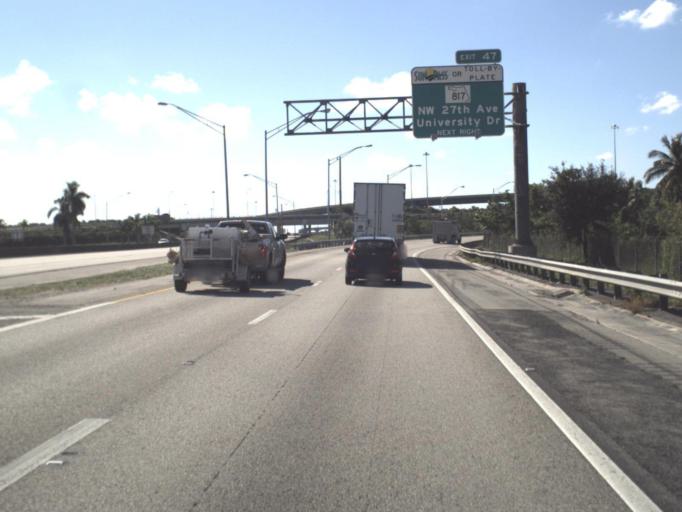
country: US
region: Florida
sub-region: Broward County
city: Miramar
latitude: 25.9767
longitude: -80.2301
